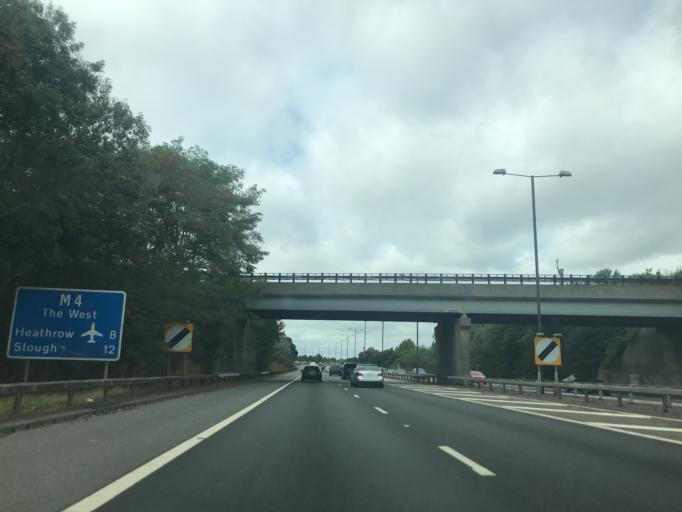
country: GB
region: England
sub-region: Greater London
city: Brentford
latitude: 51.4933
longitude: -0.3270
